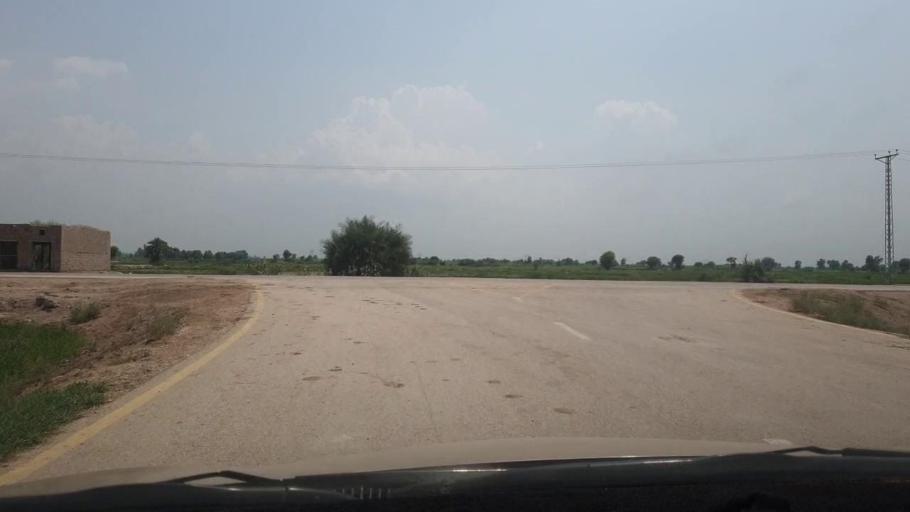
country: PK
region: Sindh
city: Naudero
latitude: 27.6947
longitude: 68.3335
